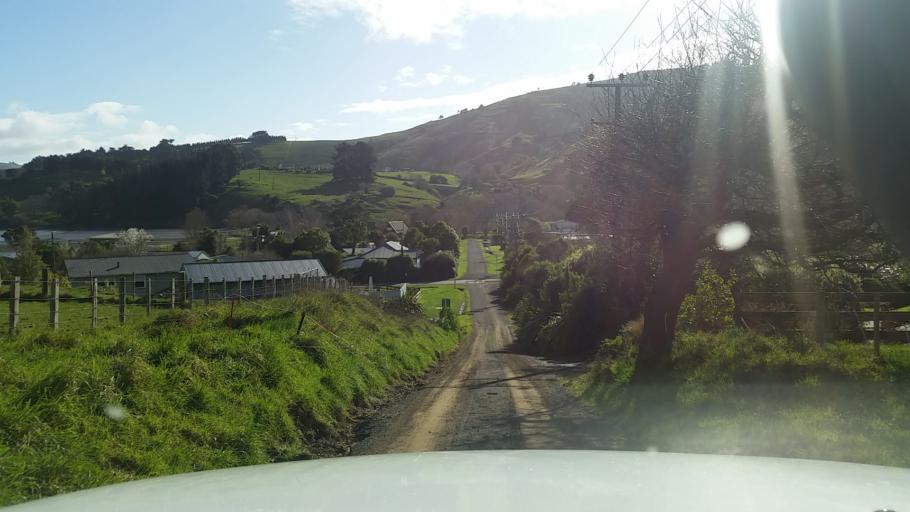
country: NZ
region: Canterbury
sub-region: Christchurch City
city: Christchurch
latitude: -43.7841
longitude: 172.9684
